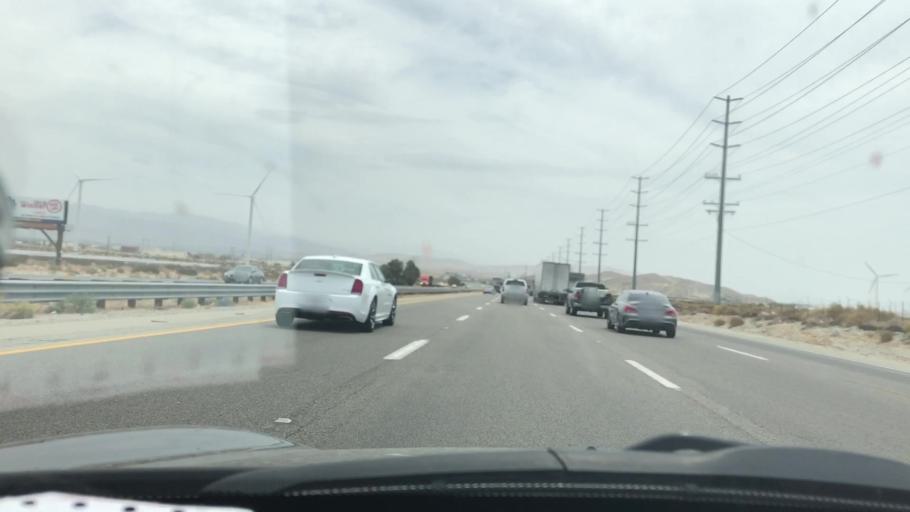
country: US
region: California
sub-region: Riverside County
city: Garnet
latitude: 33.9064
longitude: -116.5664
